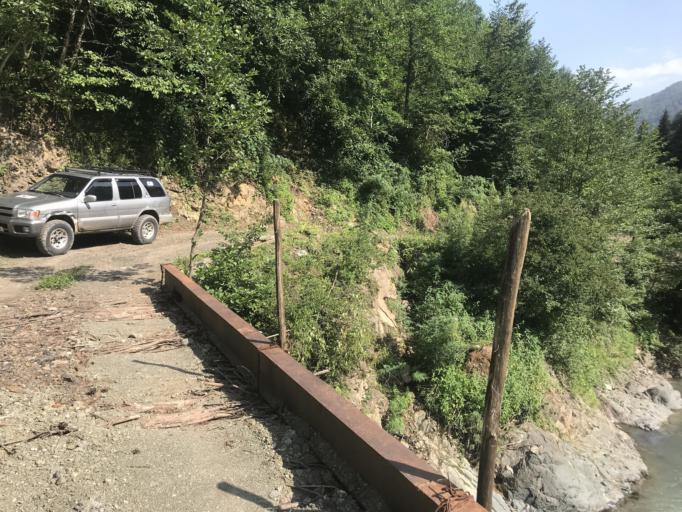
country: GE
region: Racha-Lechkhumi and Kvemo Svaneti
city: Oni
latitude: 42.6394
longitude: 43.4225
